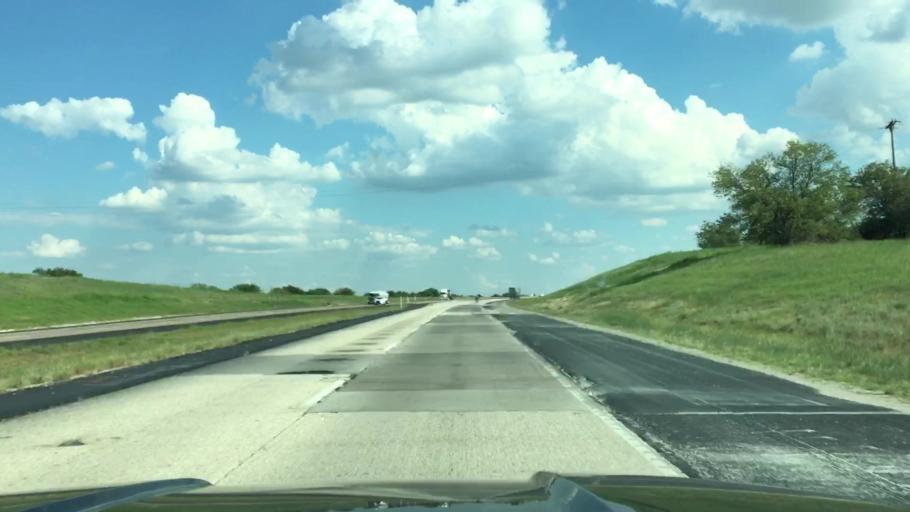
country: US
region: Texas
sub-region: Wise County
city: New Fairview
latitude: 33.1217
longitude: -97.4856
